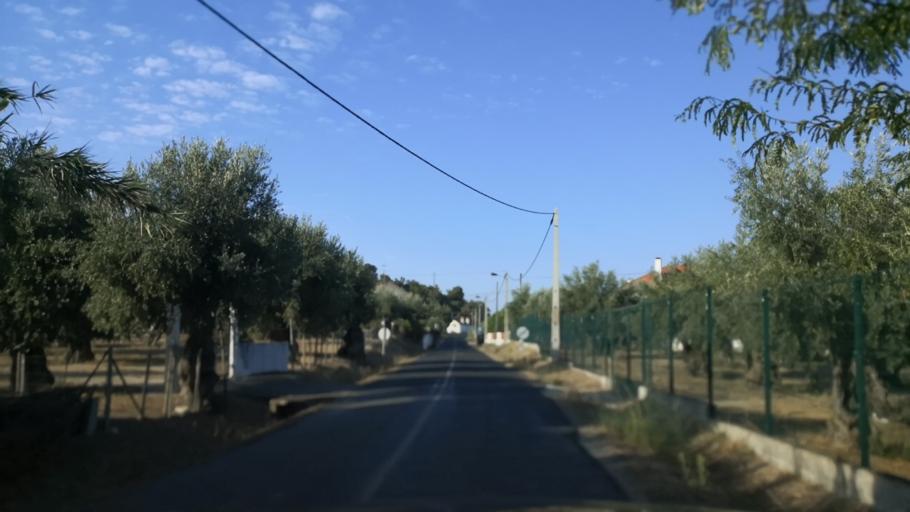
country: PT
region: Santarem
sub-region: Santarem
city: Santarem
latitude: 39.2597
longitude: -8.6678
